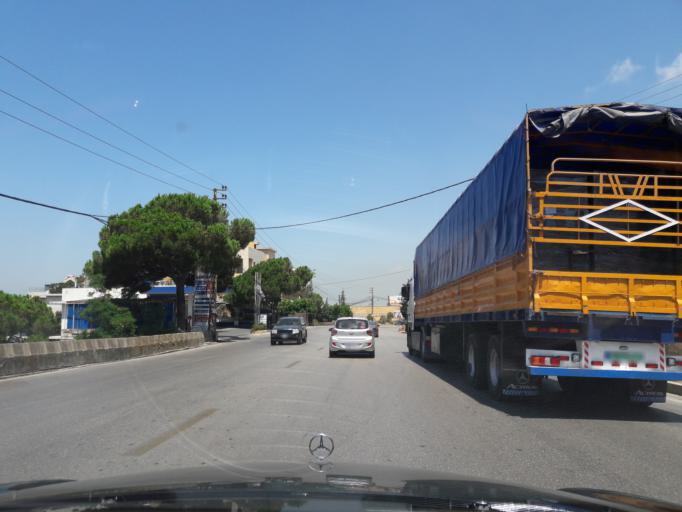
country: LB
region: Mont-Liban
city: Djounie
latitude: 33.9216
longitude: 35.6291
